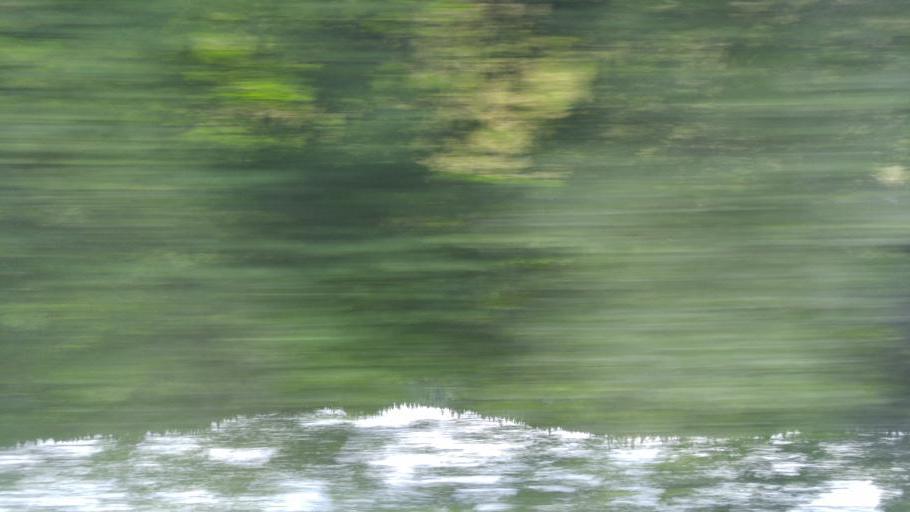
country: NO
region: Nord-Trondelag
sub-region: Levanger
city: Skogn
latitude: 63.4563
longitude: 11.3338
